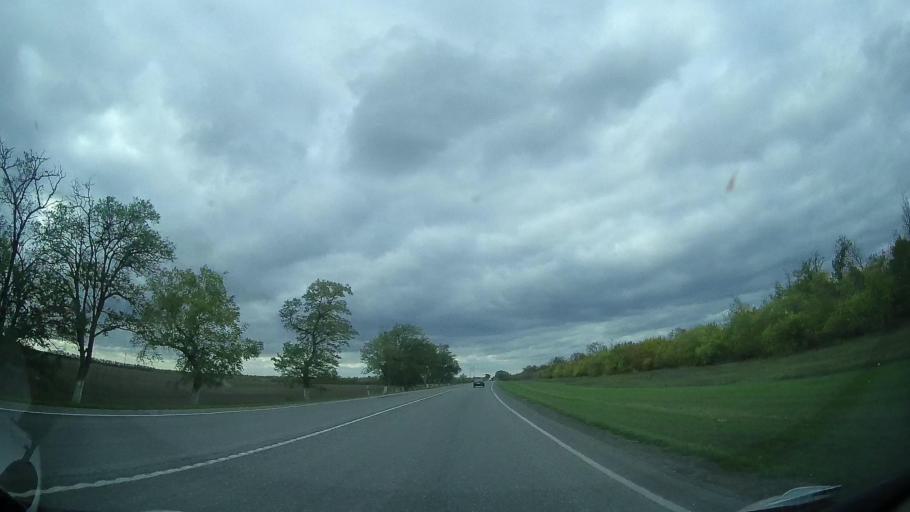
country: RU
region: Rostov
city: Zernograd
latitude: 46.8177
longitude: 40.2628
